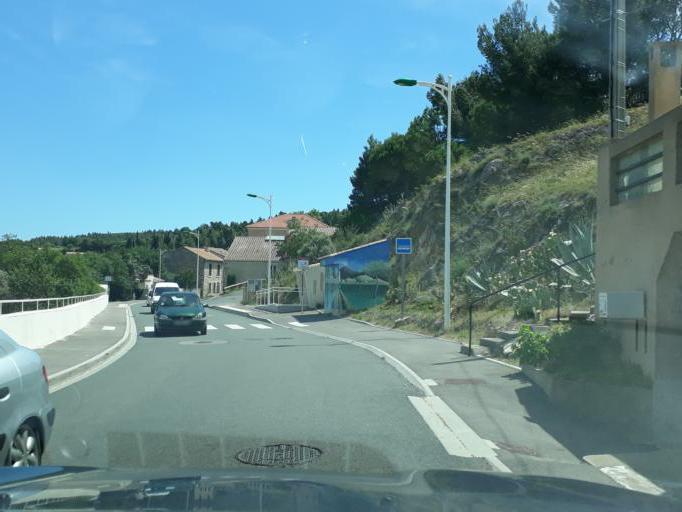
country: FR
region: Languedoc-Roussillon
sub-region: Departement de l'Aude
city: Portel-des-Corbieres
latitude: 43.0505
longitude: 2.9236
